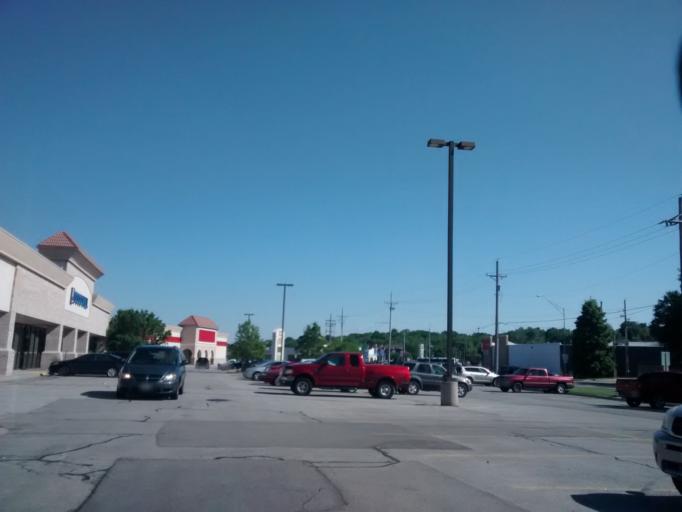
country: US
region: Nebraska
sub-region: Douglas County
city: Ralston
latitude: 41.2615
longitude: -96.0360
